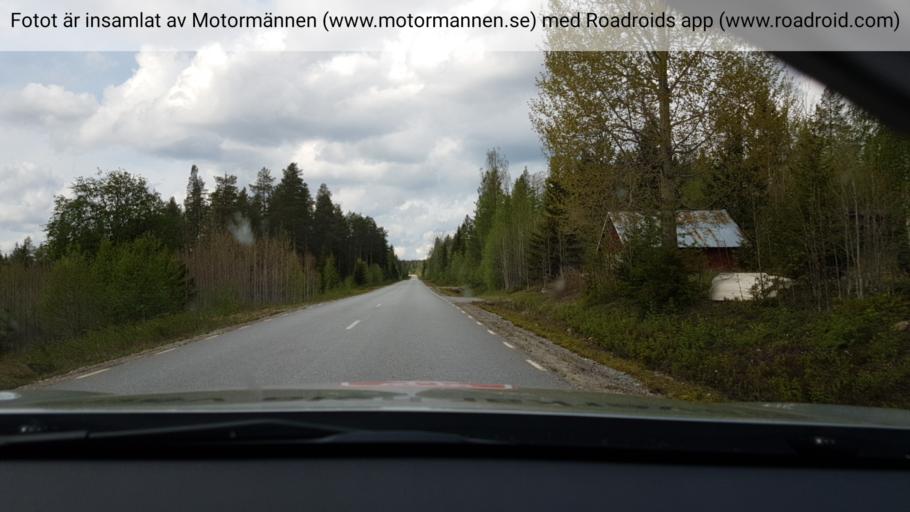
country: SE
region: Vaesternorrland
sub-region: OErnskoeldsviks Kommun
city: Ornskoldsvik
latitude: 63.8725
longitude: 18.5937
